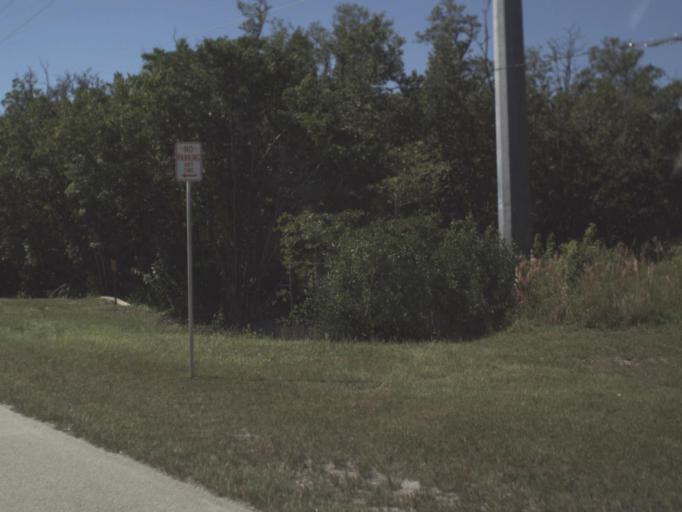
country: US
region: Florida
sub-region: Collier County
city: Marco
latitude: 25.9821
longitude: -81.7031
